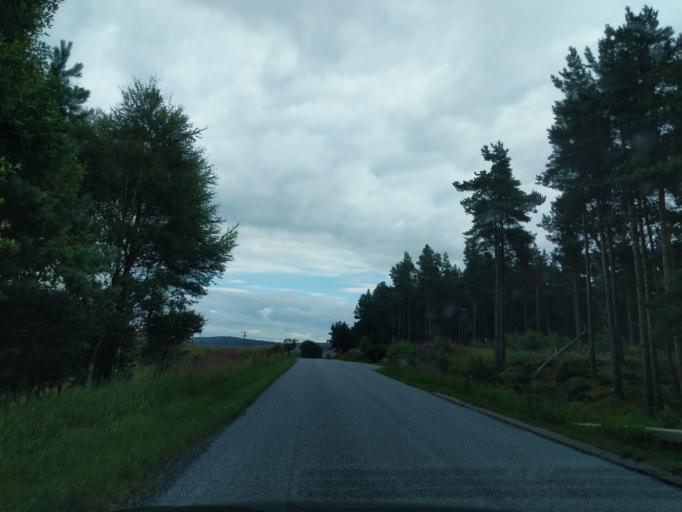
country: GB
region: Scotland
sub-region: Highland
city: Grantown on Spey
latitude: 57.3065
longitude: -3.7393
